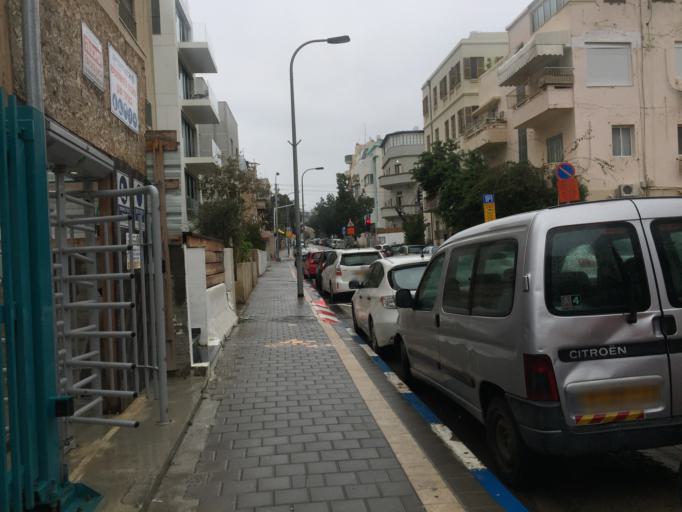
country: IL
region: Tel Aviv
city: Tel Aviv
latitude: 32.0713
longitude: 34.7664
